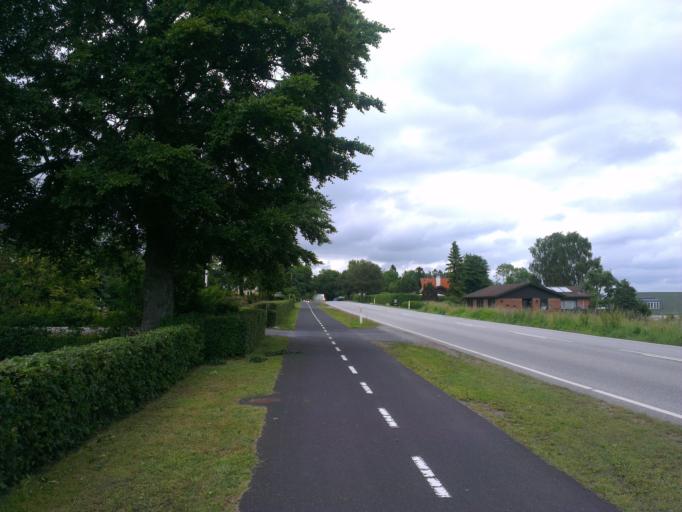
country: DK
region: Capital Region
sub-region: Frederikssund Kommune
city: Skibby
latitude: 55.6854
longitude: 11.9474
